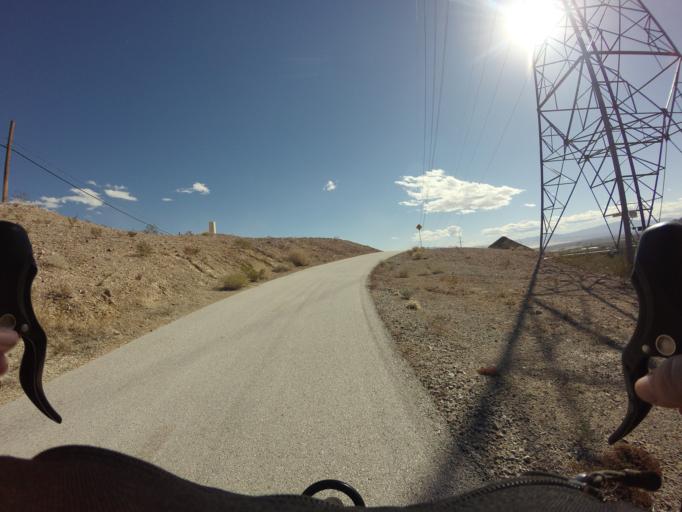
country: US
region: Nevada
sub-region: Clark County
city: Boulder City
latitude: 35.9706
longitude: -114.9088
